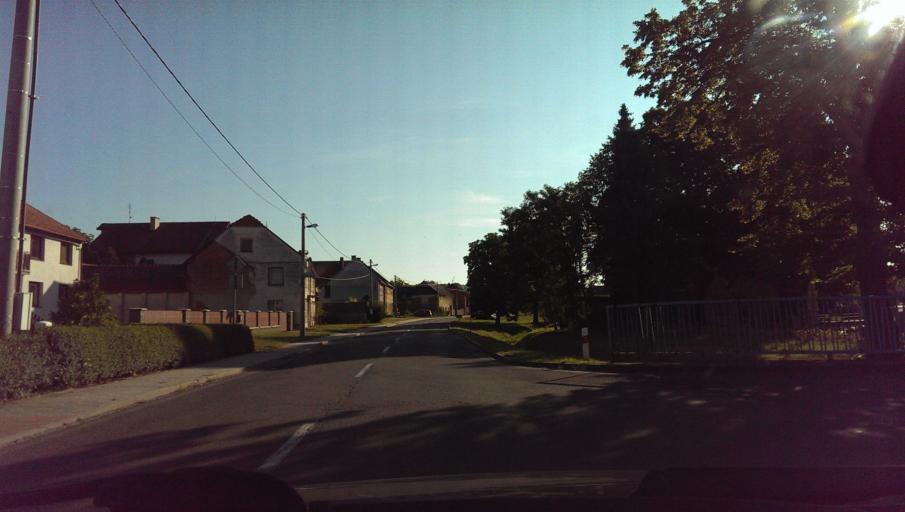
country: CZ
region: Zlin
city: Bystrice pod Hostynem
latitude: 49.4674
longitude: 17.7113
